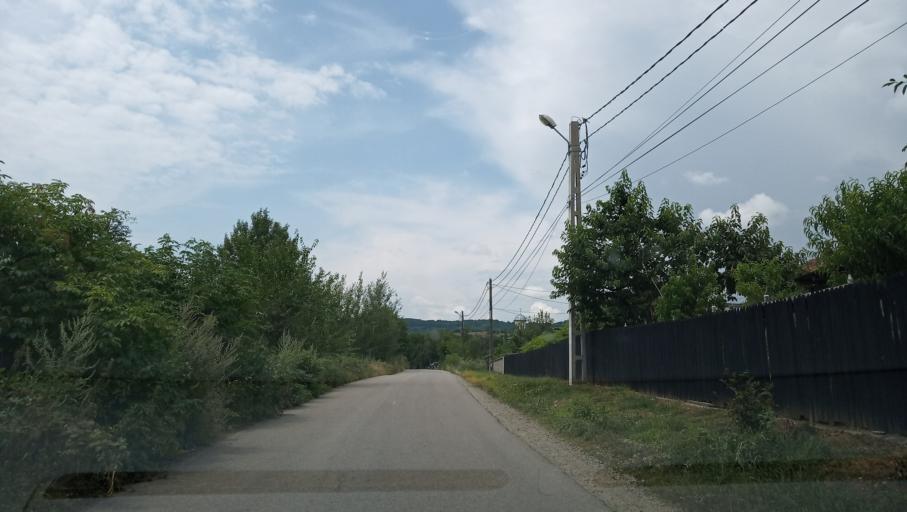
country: RO
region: Gorj
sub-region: Comuna Bumbesti-Jiu
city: Bumbesti-Jiu
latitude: 45.1759
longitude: 23.3639
